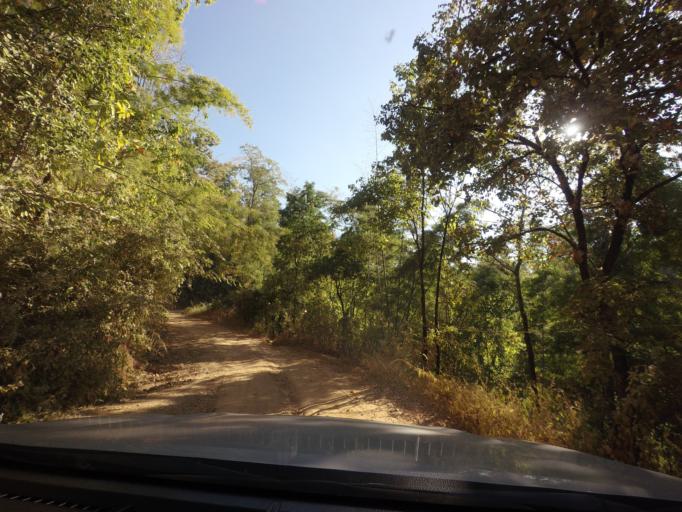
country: TH
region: Lampang
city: Chae Hom
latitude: 18.6145
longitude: 99.6517
